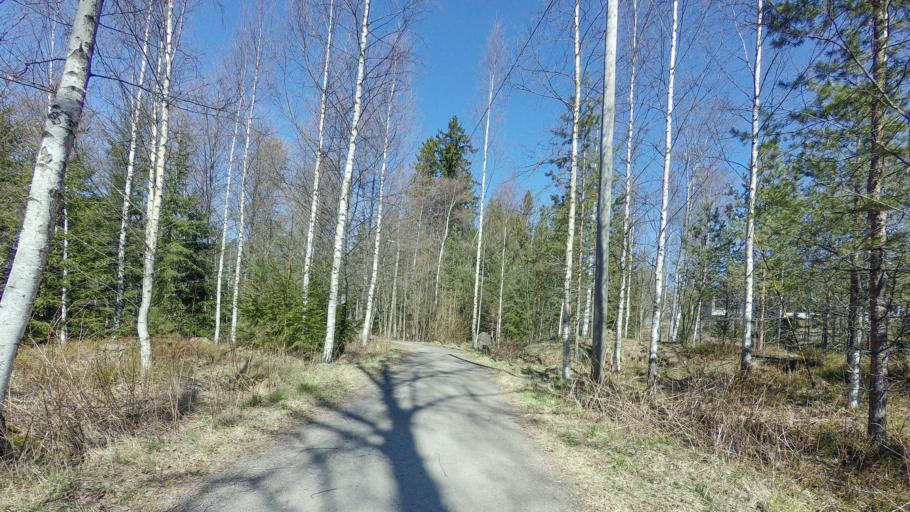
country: FI
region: Uusimaa
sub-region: Helsinki
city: Helsinki
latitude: 60.1647
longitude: 25.0381
